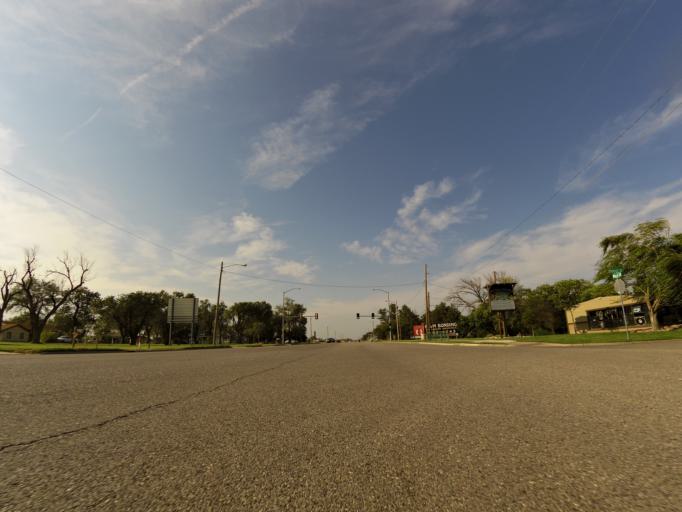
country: US
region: Kansas
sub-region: Reno County
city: South Hutchinson
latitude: 38.0156
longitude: -97.9401
